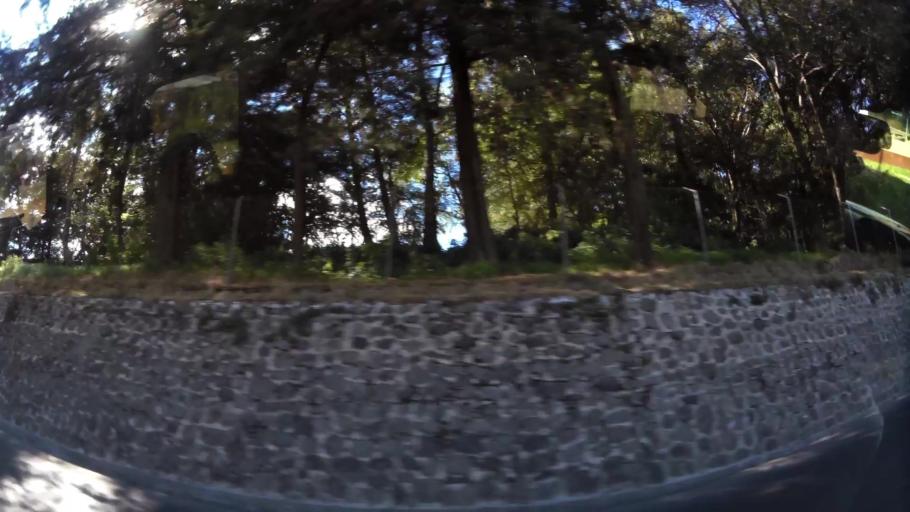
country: GT
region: Solola
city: Solola
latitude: 14.7900
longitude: -91.1828
